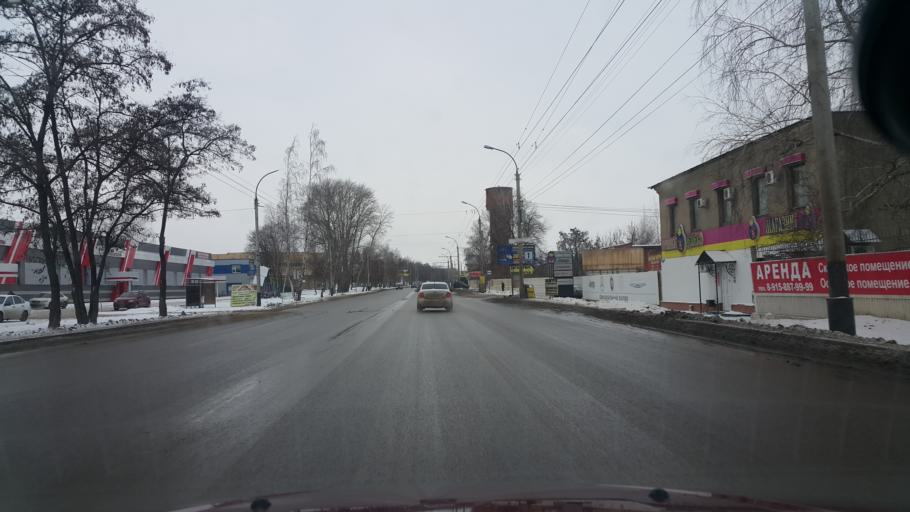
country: RU
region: Tambov
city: Tambov
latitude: 52.7339
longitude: 41.3981
